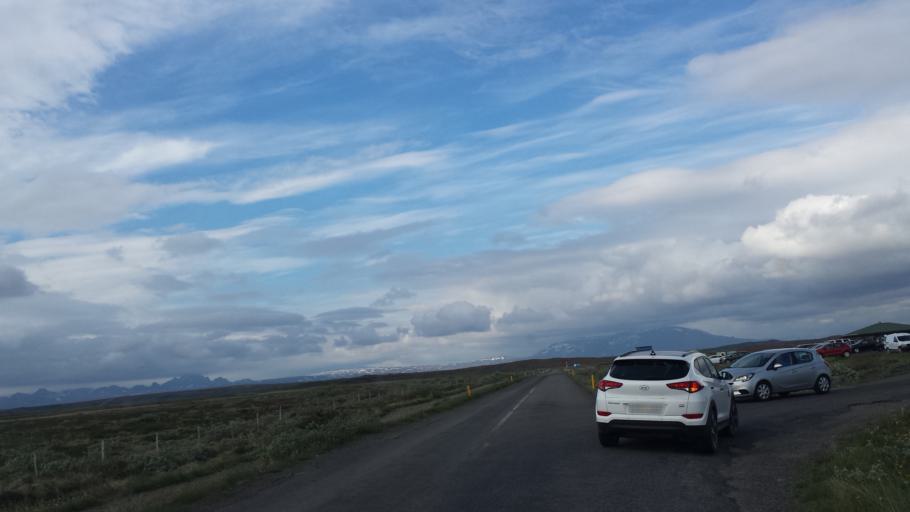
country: IS
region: South
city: Vestmannaeyjar
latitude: 64.3247
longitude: -20.1327
